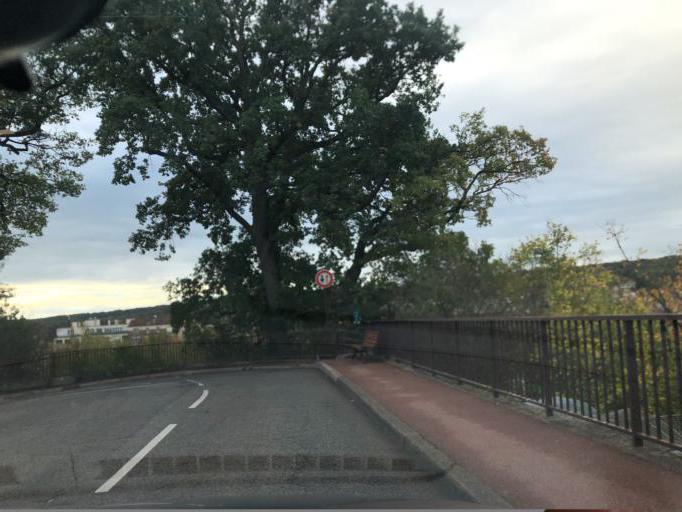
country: FR
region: Ile-de-France
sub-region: Departement des Hauts-de-Seine
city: Chaville
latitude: 48.8060
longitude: 2.1777
